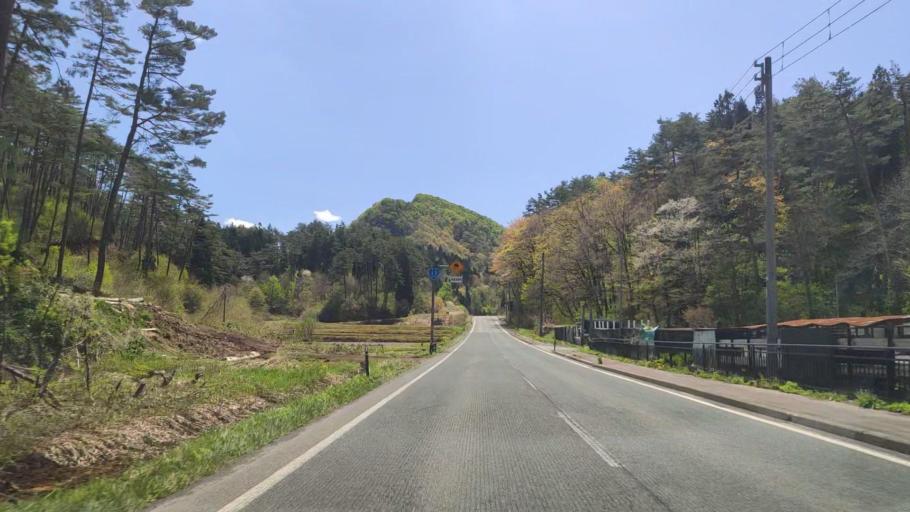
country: JP
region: Yamagata
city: Shinjo
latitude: 38.9034
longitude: 140.3275
